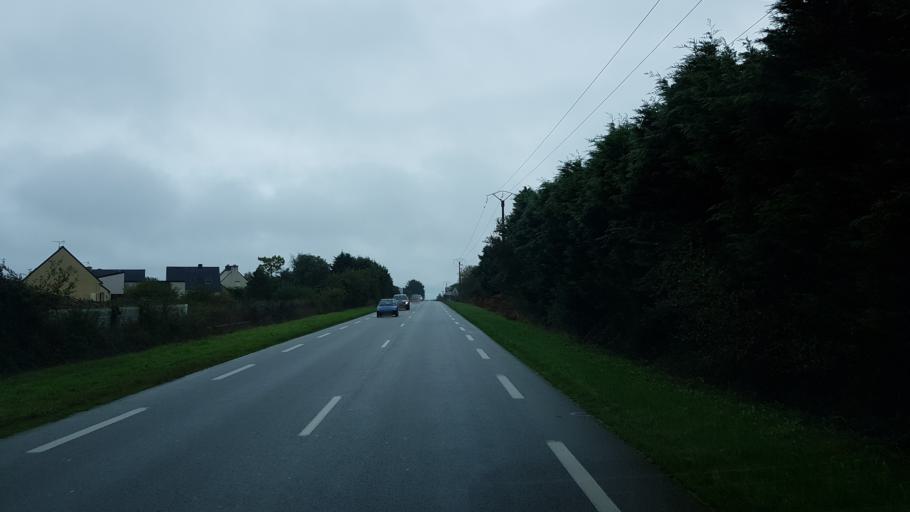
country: FR
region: Brittany
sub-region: Departement du Morbihan
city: Sarzeau
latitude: 47.5254
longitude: -2.7911
